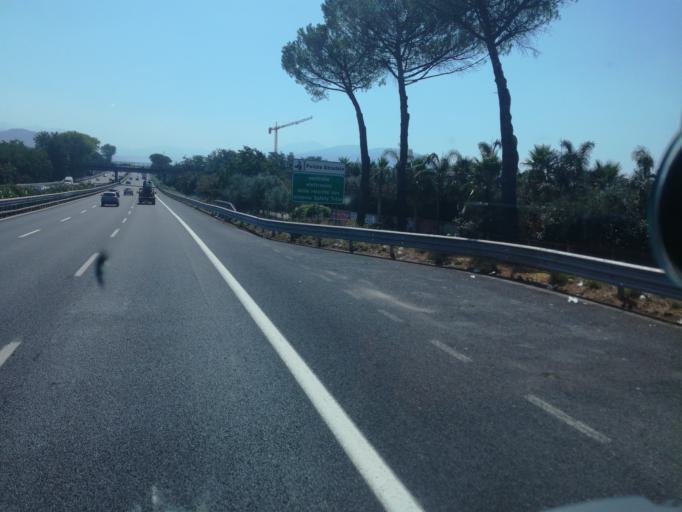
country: IT
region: Campania
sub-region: Provincia di Napoli
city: Saviano
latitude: 40.9192
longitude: 14.5106
